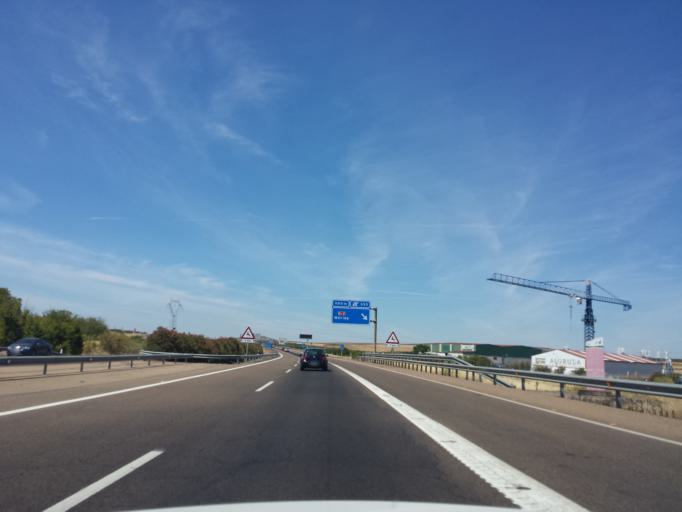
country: ES
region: Extremadura
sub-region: Provincia de Badajoz
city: Trujillanos
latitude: 38.9485
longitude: -6.2716
